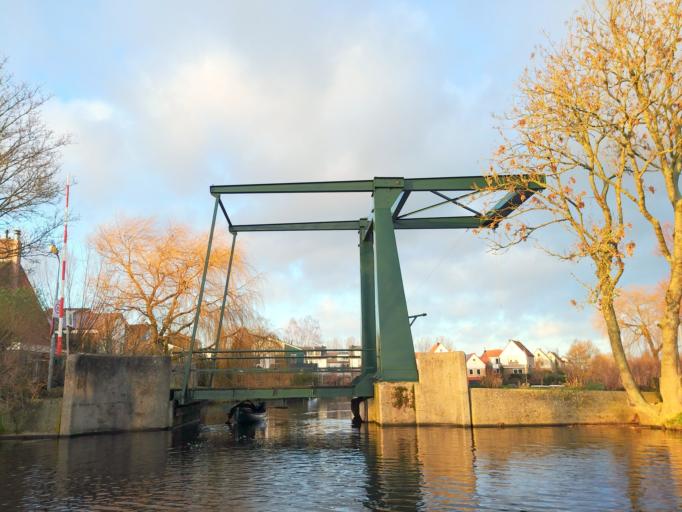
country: NL
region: North Holland
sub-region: Gemeente Zaanstad
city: Zaanstad
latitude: 52.4614
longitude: 4.7676
